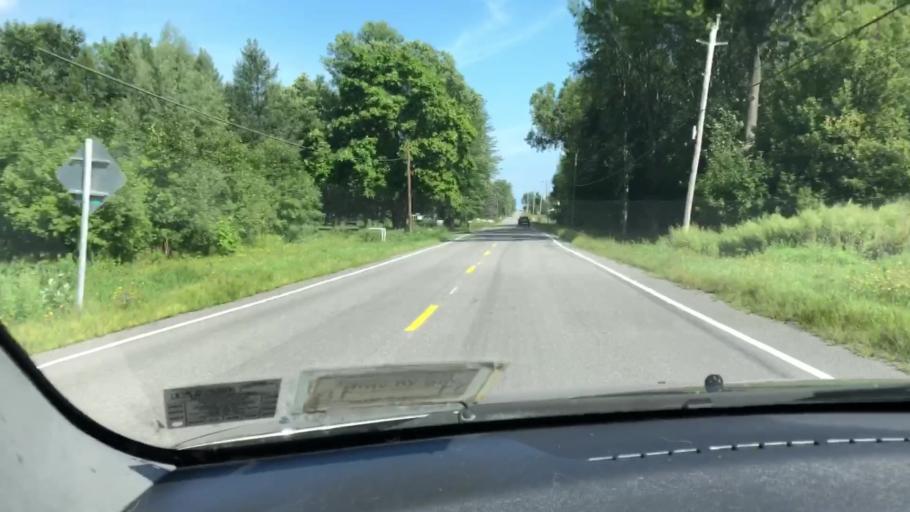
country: US
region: New York
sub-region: Wayne County
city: Macedon
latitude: 43.0981
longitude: -77.3206
